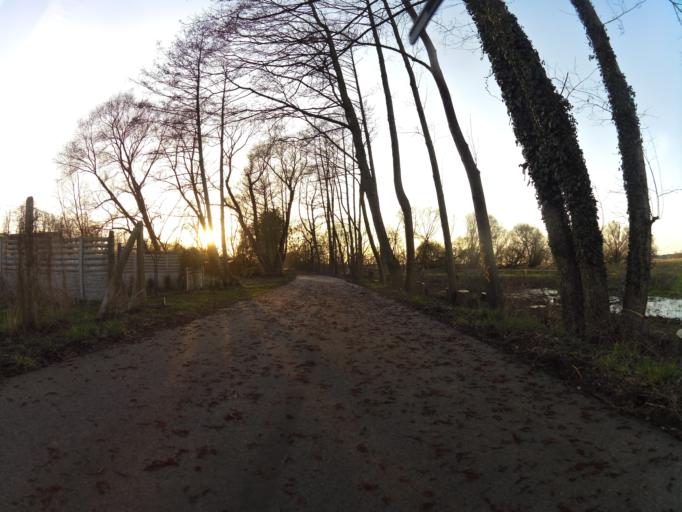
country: PL
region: West Pomeranian Voivodeship
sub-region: Powiat policki
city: Nowe Warpno
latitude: 53.7222
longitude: 14.3061
